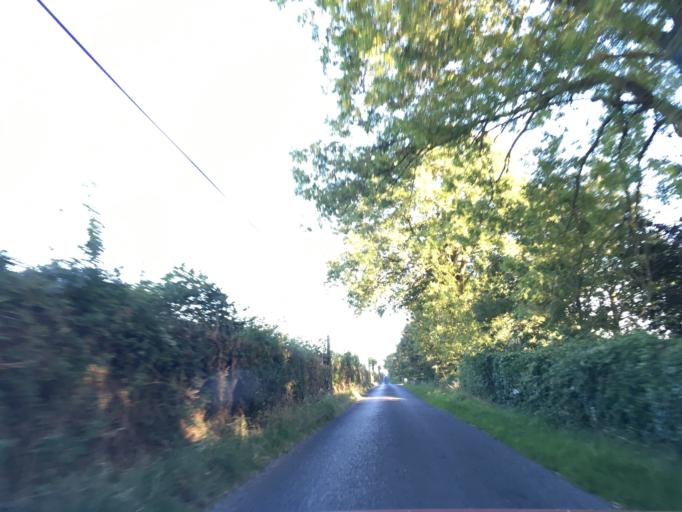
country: IE
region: Munster
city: Cashel
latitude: 52.5052
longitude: -7.9327
